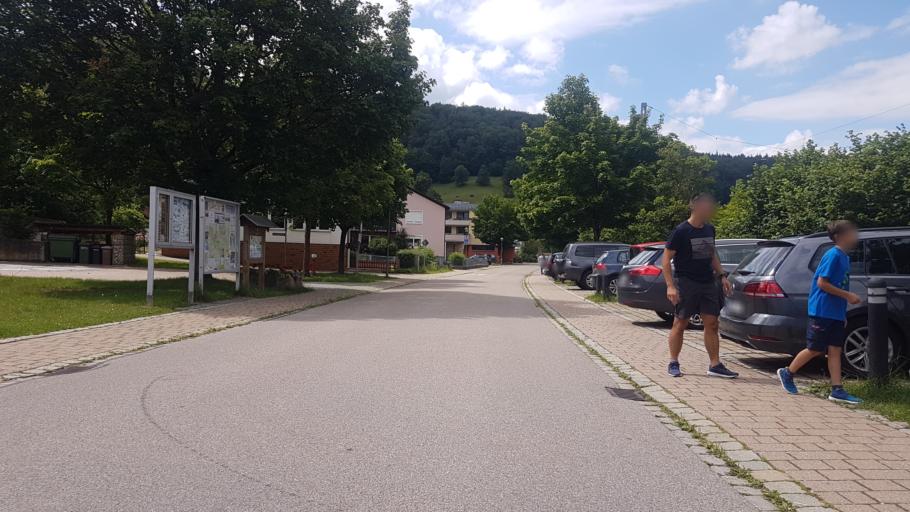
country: DE
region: Bavaria
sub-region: Regierungsbezirk Mittelfranken
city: Solnhofen
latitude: 48.8924
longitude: 10.9928
